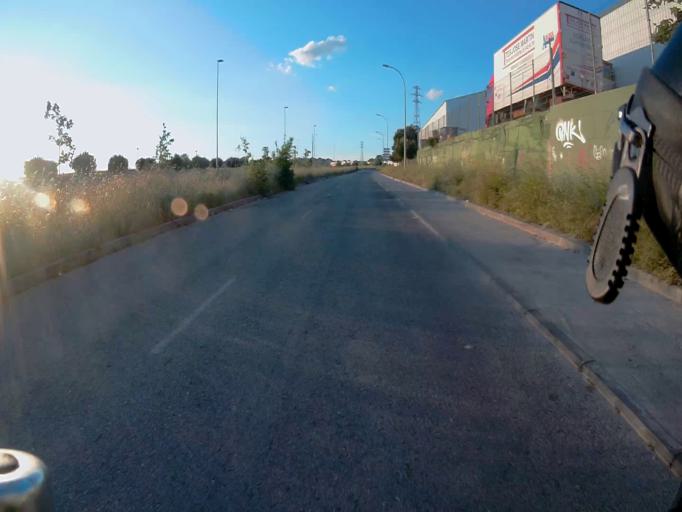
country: ES
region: Madrid
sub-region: Provincia de Madrid
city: Alcorcon
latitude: 40.3309
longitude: -3.8186
